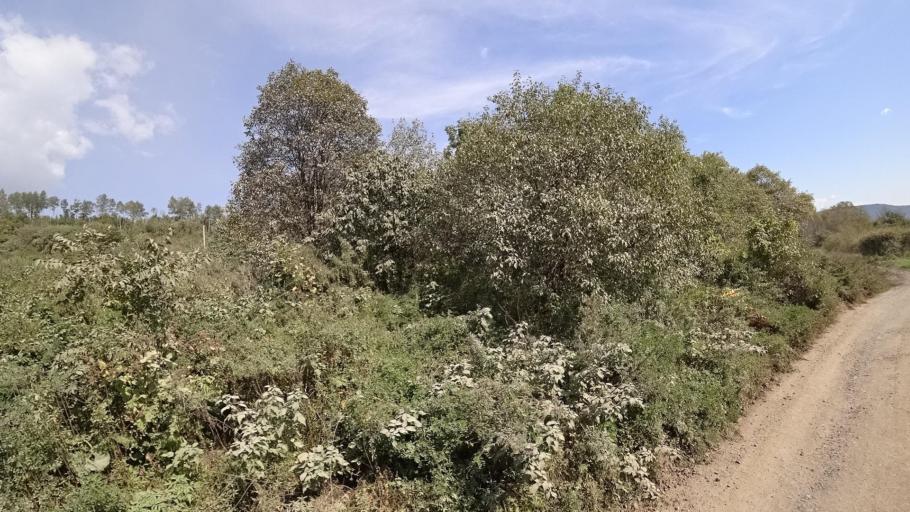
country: RU
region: Jewish Autonomous Oblast
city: Londoko
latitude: 49.0080
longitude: 131.9136
